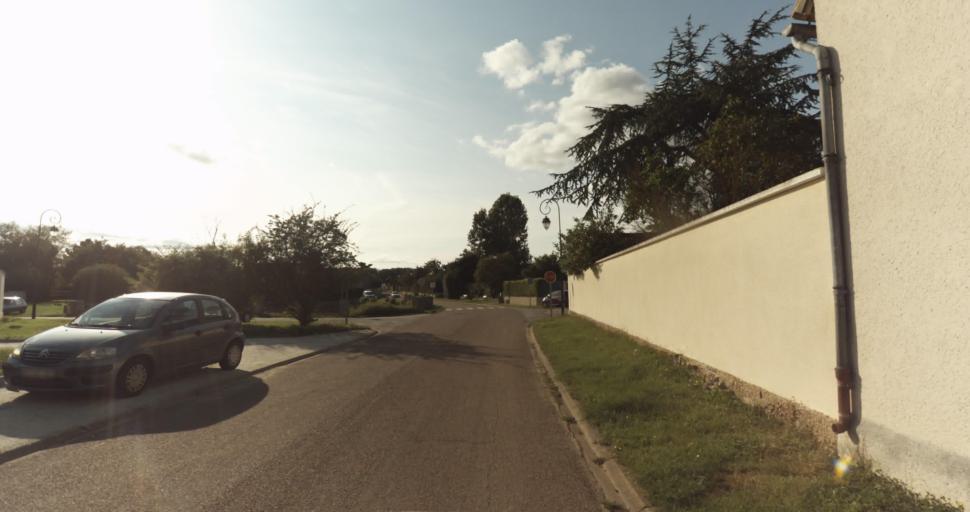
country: FR
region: Haute-Normandie
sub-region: Departement de l'Eure
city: Marcilly-sur-Eure
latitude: 48.9057
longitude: 1.3130
